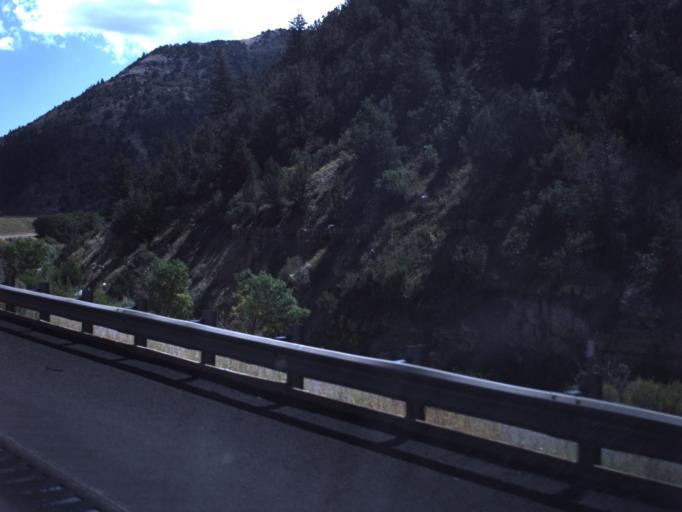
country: US
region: Utah
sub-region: Sevier County
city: Salina
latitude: 38.8843
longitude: -111.5997
